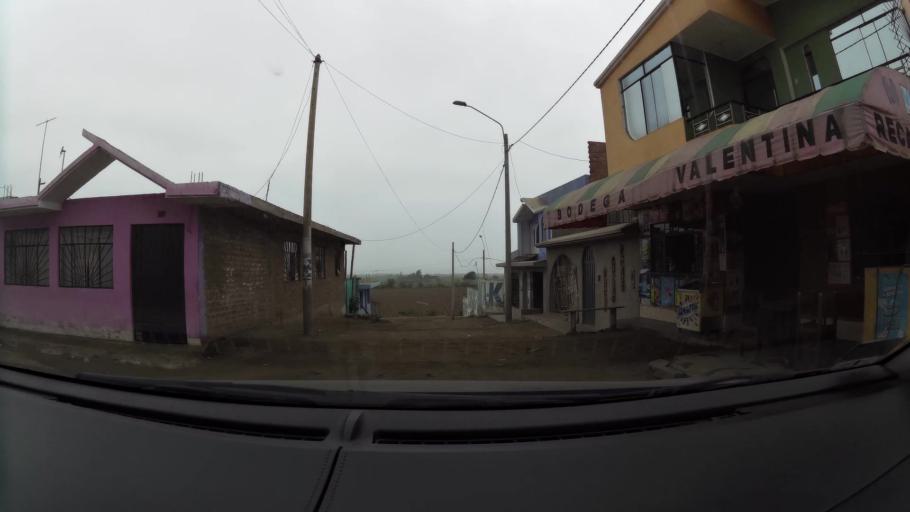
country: PE
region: Lima
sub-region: Provincia de Huaral
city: Chancay
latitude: -11.5967
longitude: -77.2554
